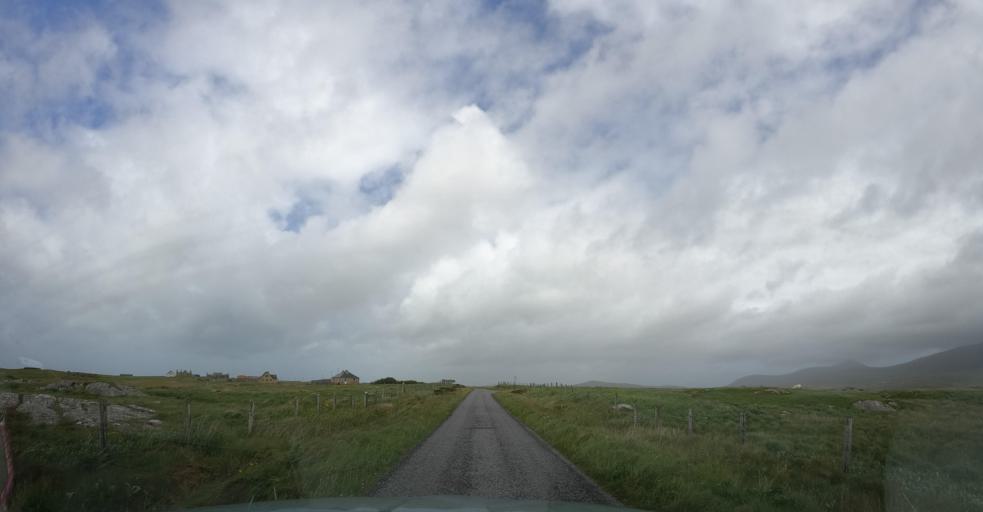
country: GB
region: Scotland
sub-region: Eilean Siar
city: Isle of South Uist
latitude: 57.2548
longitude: -7.4048
